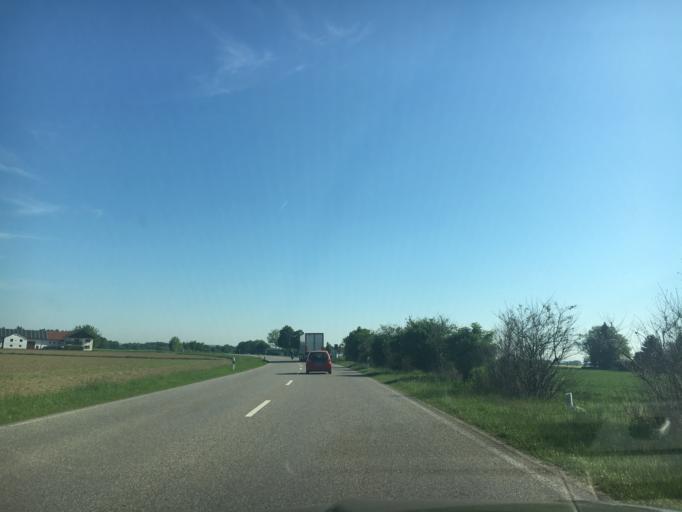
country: DE
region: Bavaria
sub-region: Upper Bavaria
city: Unterneukirchen
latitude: 48.1919
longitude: 12.6411
